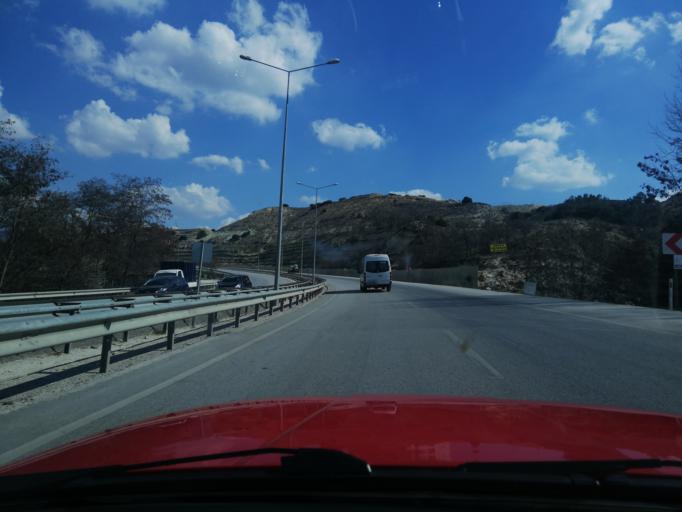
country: TR
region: Burdur
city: Burdur
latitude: 37.7023
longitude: 30.3076
